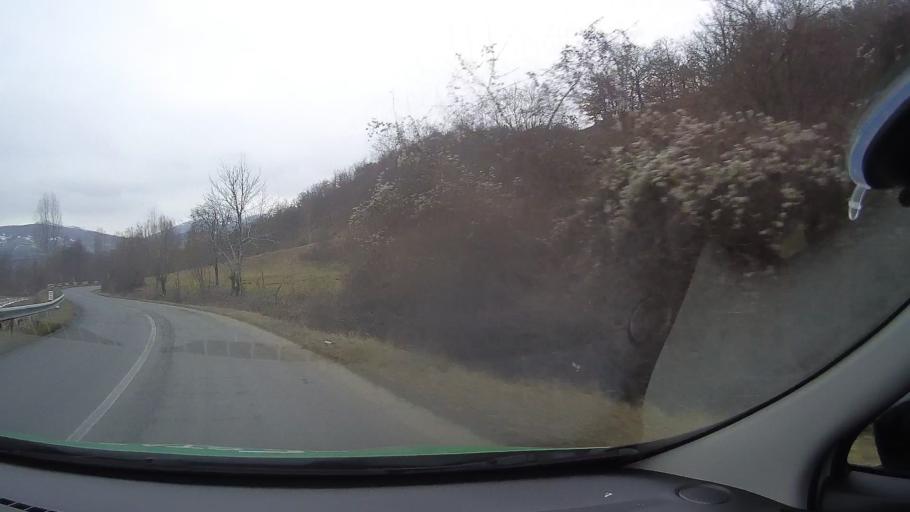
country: RO
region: Alba
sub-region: Comuna Metes
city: Metes
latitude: 46.1029
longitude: 23.4524
